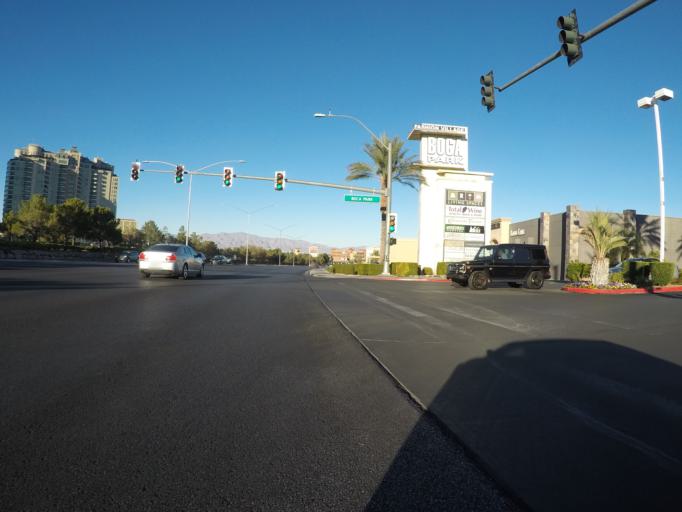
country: US
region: Nevada
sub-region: Clark County
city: Summerlin South
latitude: 36.1638
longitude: -115.2907
